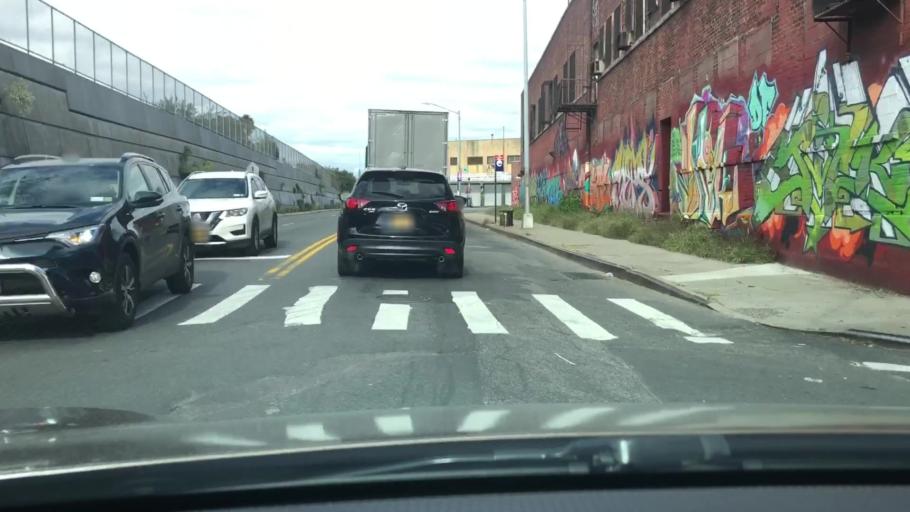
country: US
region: New York
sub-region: Queens County
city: Long Island City
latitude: 40.7197
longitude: -73.9114
